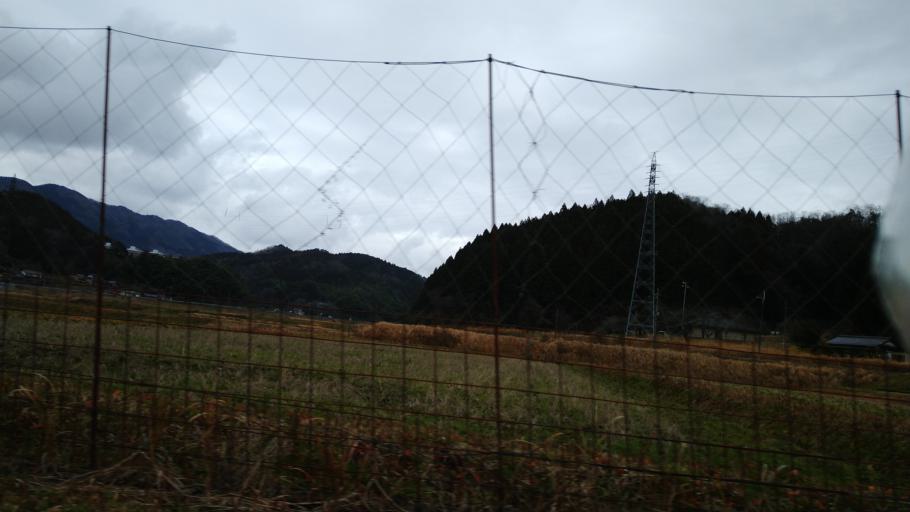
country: JP
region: Kyoto
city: Ayabe
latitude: 35.3333
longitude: 135.3495
